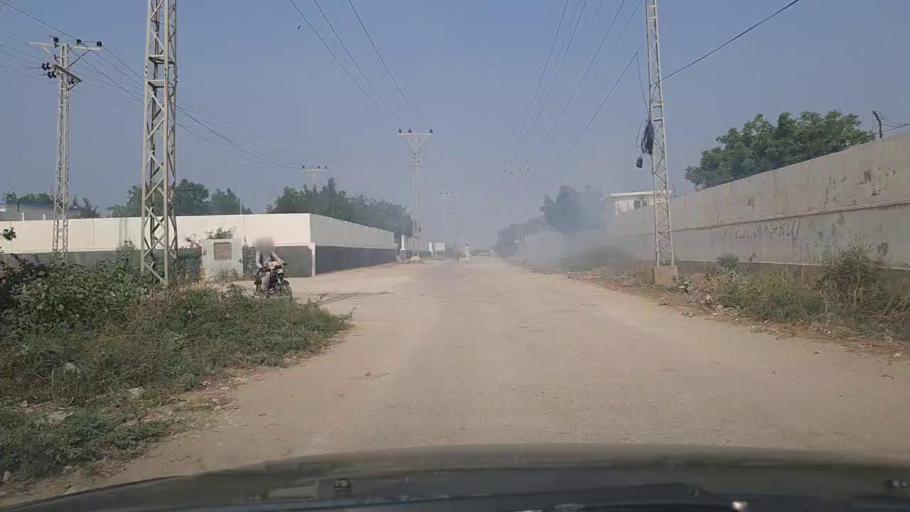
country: PK
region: Sindh
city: Thatta
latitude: 24.7507
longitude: 67.8974
